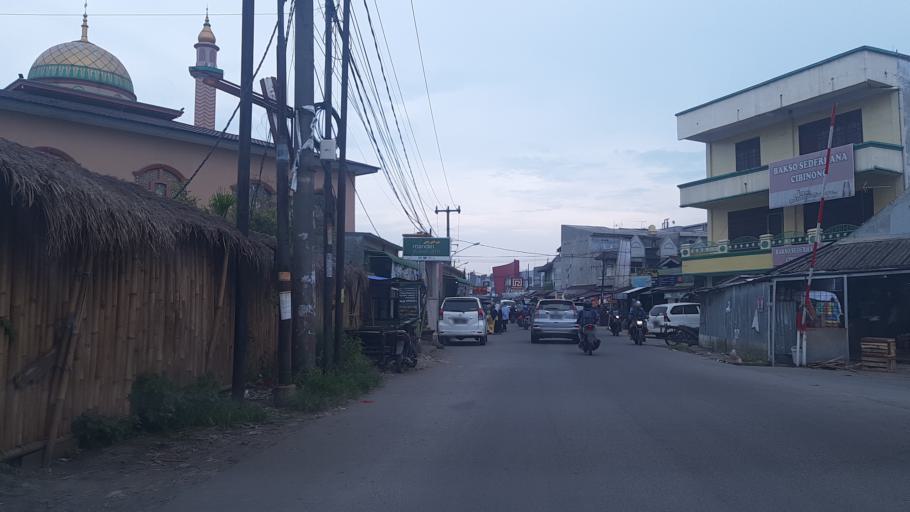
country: ID
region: West Java
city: Cibinong
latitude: -6.4676
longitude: 106.8564
